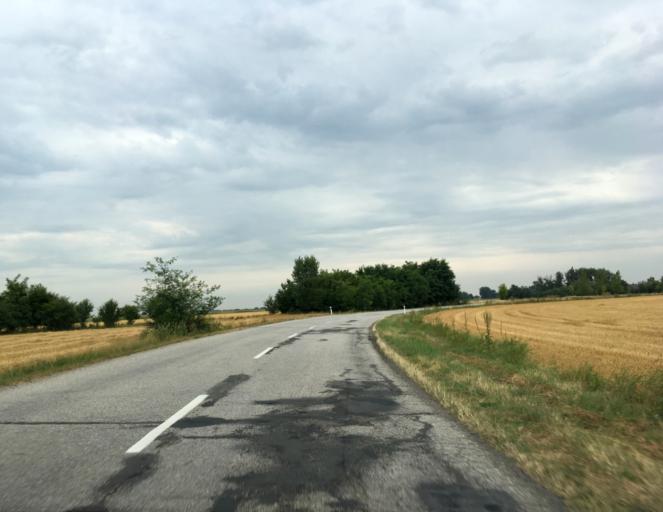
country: SK
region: Nitriansky
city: Kolarovo
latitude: 47.8864
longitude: 17.9243
